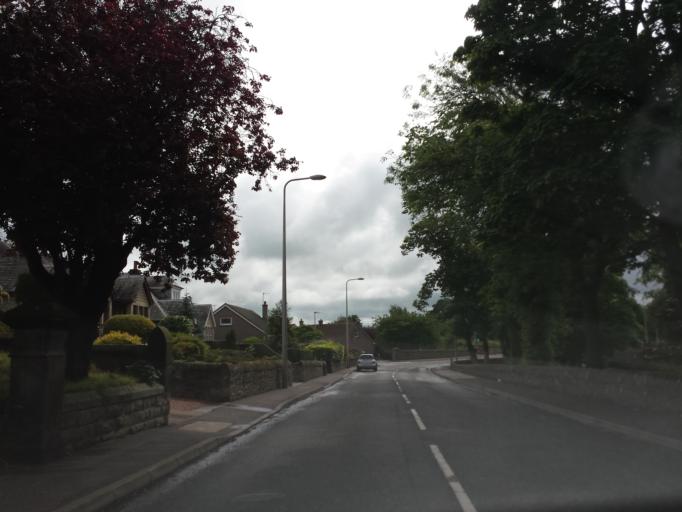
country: GB
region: Scotland
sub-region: Fife
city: Cupar
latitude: 56.3204
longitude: -3.0059
